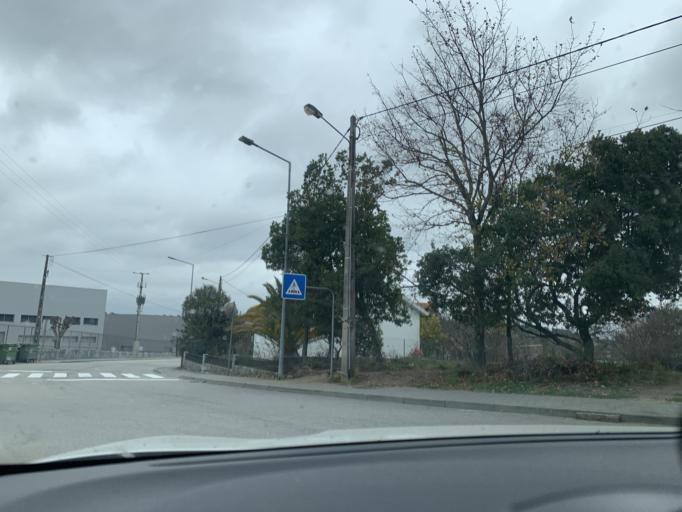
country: PT
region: Viseu
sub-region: Mangualde
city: Mangualde
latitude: 40.6123
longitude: -7.7672
